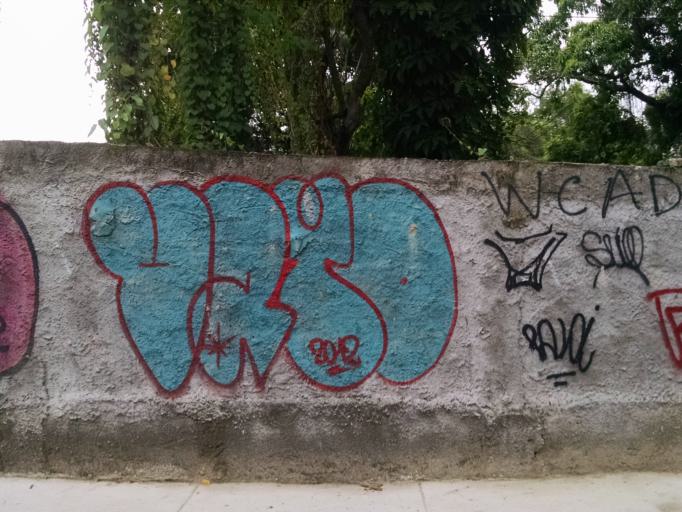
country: BR
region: Rio de Janeiro
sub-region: Rio De Janeiro
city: Rio de Janeiro
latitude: -22.9247
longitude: -43.1883
